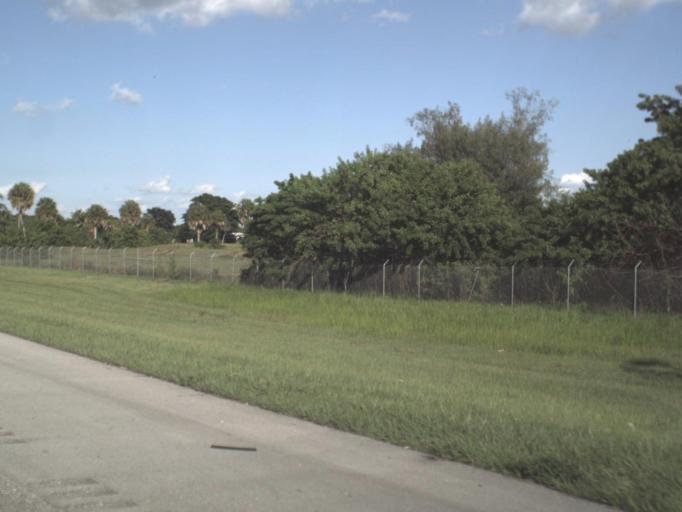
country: US
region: Florida
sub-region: Broward County
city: Lauderdale Lakes
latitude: 26.1840
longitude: -80.2170
